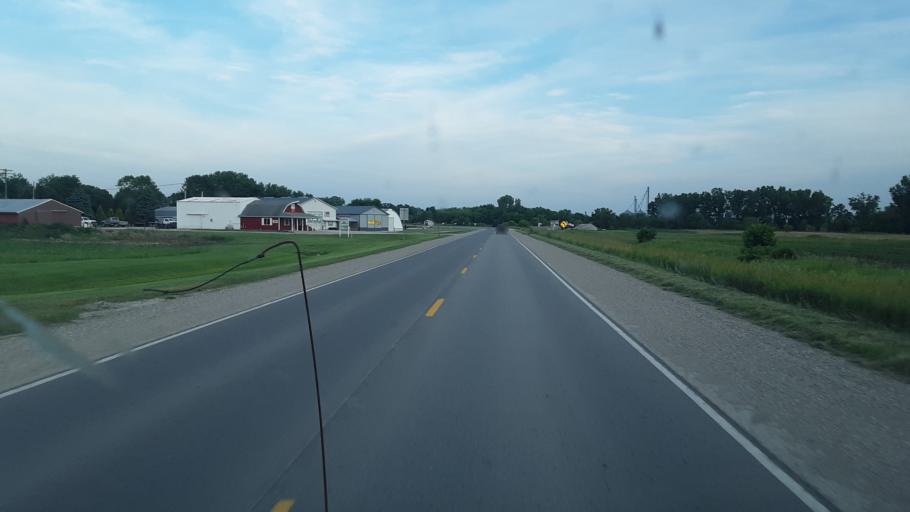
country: US
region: Iowa
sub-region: Benton County
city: Belle Plaine
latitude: 41.9012
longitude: -92.2924
